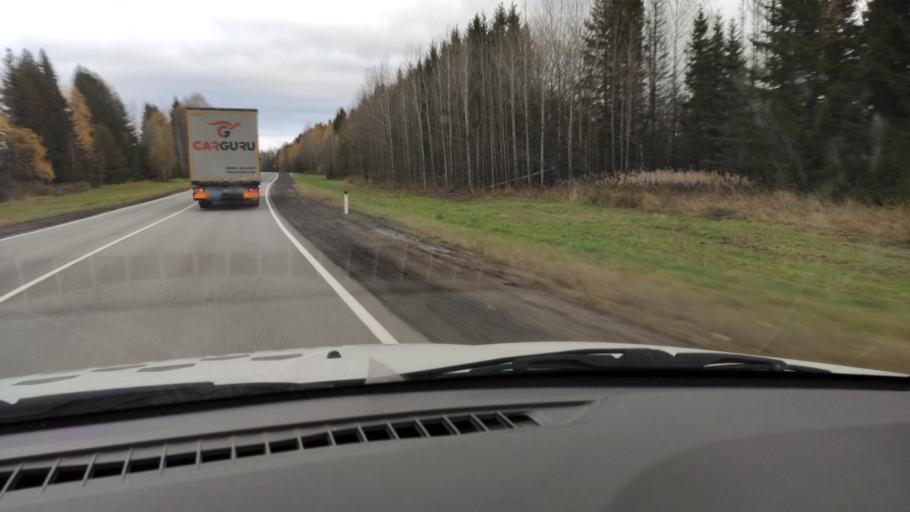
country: RU
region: Kirov
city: Belaya Kholunitsa
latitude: 58.8172
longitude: 50.5947
